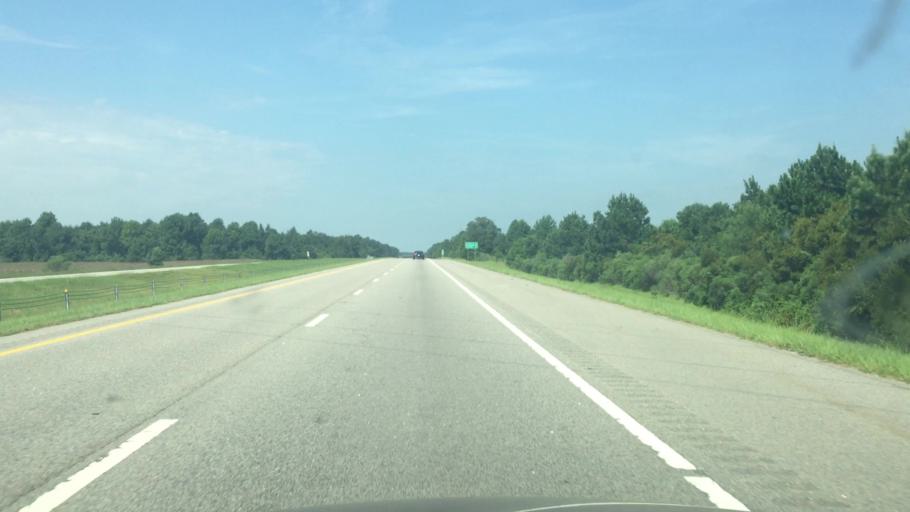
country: US
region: North Carolina
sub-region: Robeson County
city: Pembroke
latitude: 34.5988
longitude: -79.1475
